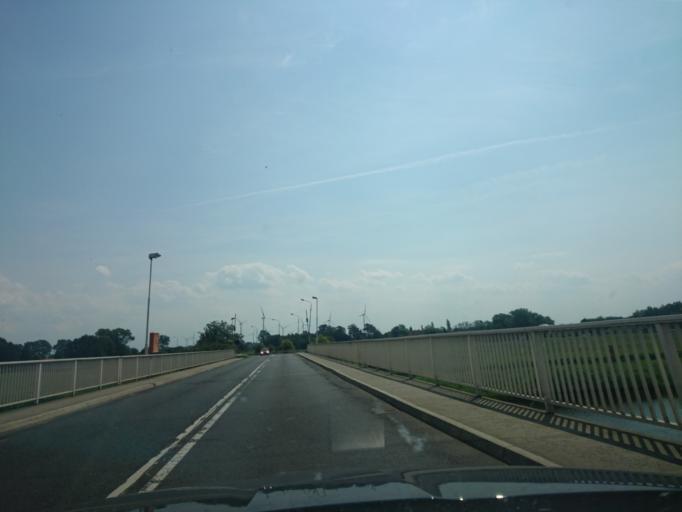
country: PL
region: West Pomeranian Voivodeship
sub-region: Powiat kamienski
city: Wolin
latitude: 53.8435
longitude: 14.6198
